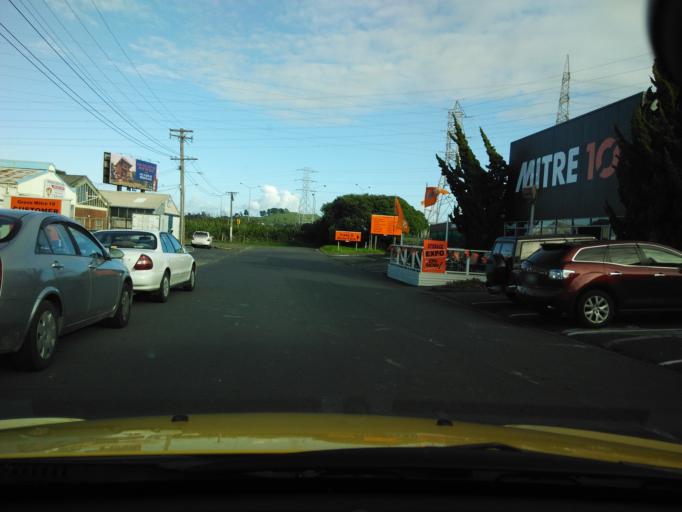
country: NZ
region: Auckland
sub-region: Auckland
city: Mangere
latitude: -36.9261
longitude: 174.7795
